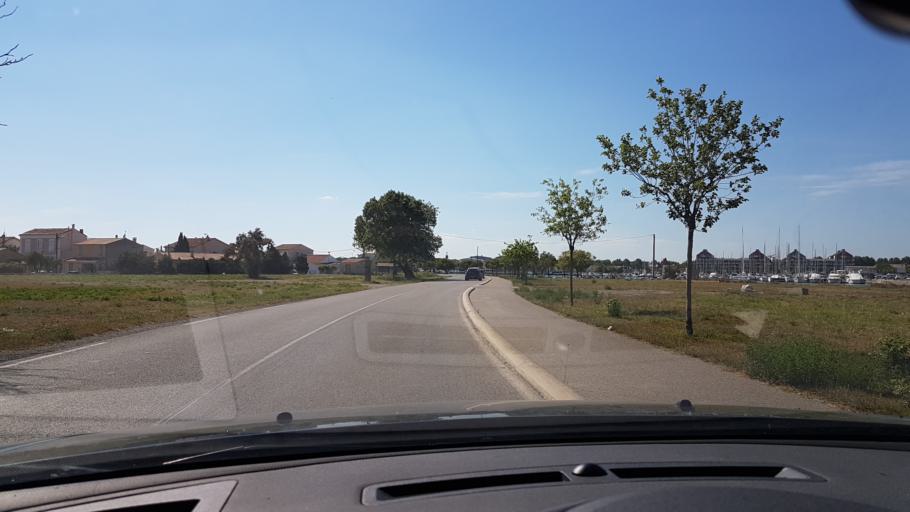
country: FR
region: Provence-Alpes-Cote d'Azur
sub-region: Departement des Bouches-du-Rhone
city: Port-Saint-Louis-du-Rhone
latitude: 43.3836
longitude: 4.8135
